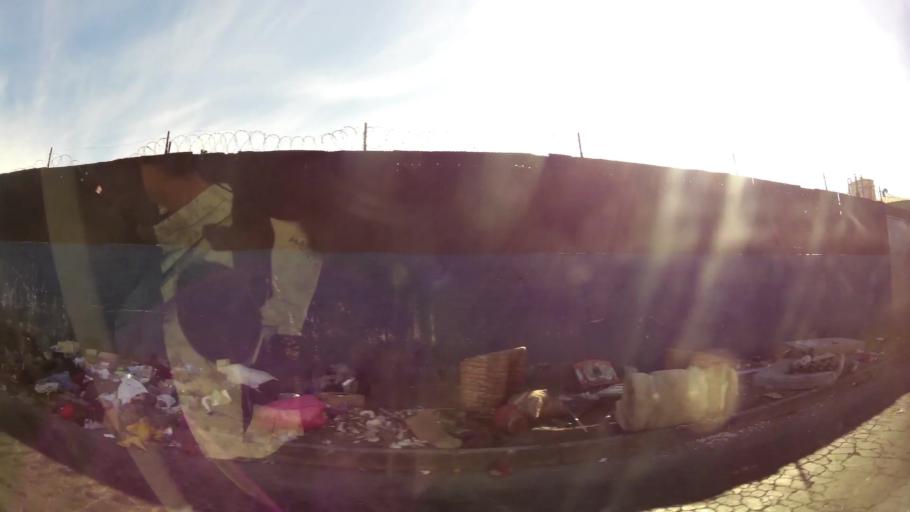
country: CL
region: Santiago Metropolitan
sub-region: Provincia de Santiago
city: Lo Prado
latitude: -33.4627
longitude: -70.6956
